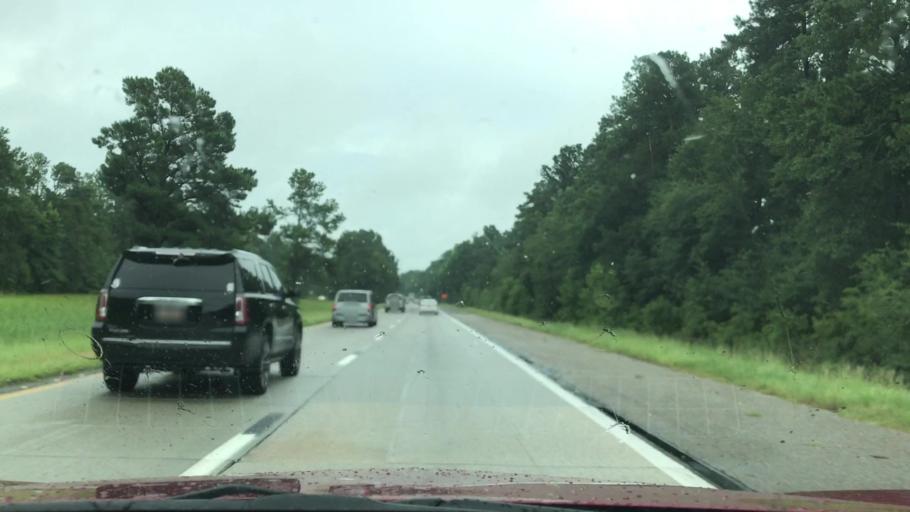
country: US
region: South Carolina
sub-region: Dorchester County
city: Ridgeville
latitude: 33.1874
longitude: -80.3864
